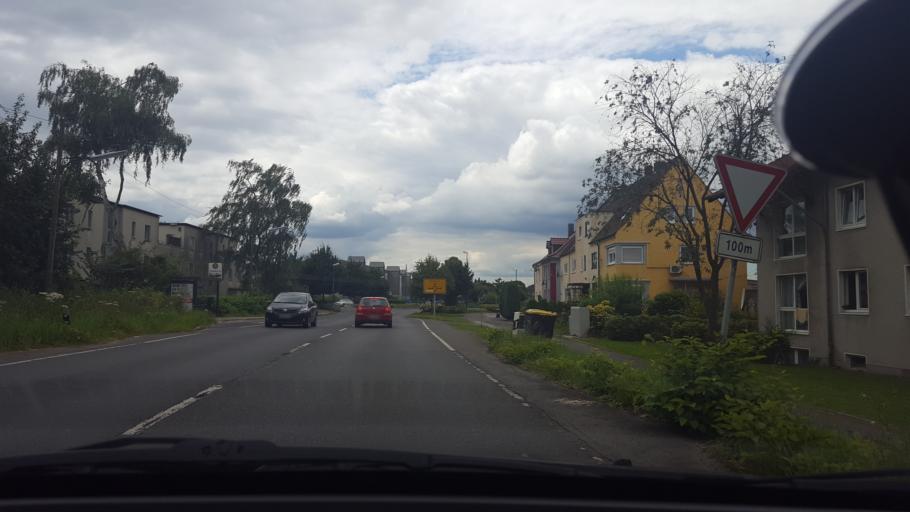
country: DE
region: North Rhine-Westphalia
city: Oer-Erkenschwick
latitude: 51.6245
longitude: 7.2360
